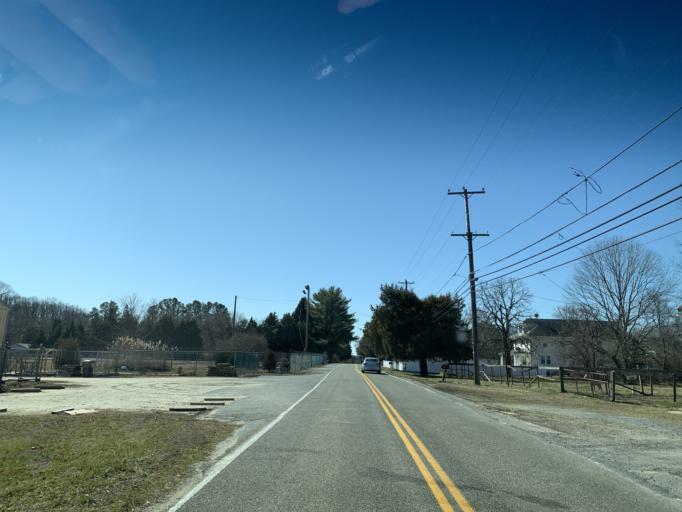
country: US
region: Maryland
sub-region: Cecil County
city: Elkton
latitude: 39.5198
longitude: -75.8212
